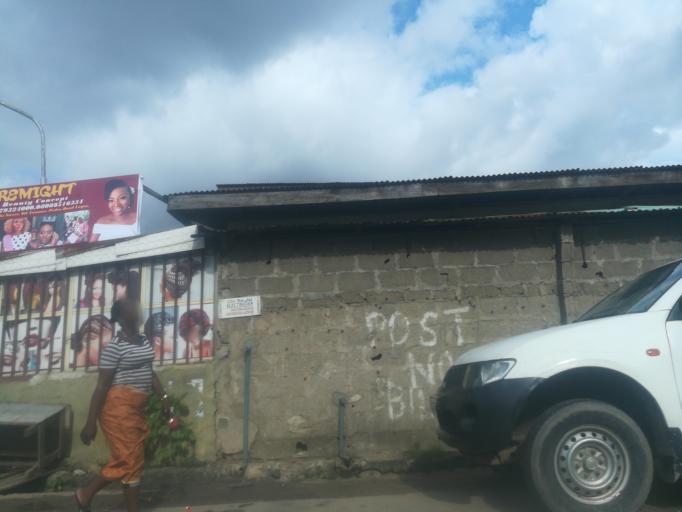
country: NG
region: Lagos
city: Somolu
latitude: 6.5450
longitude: 3.3760
